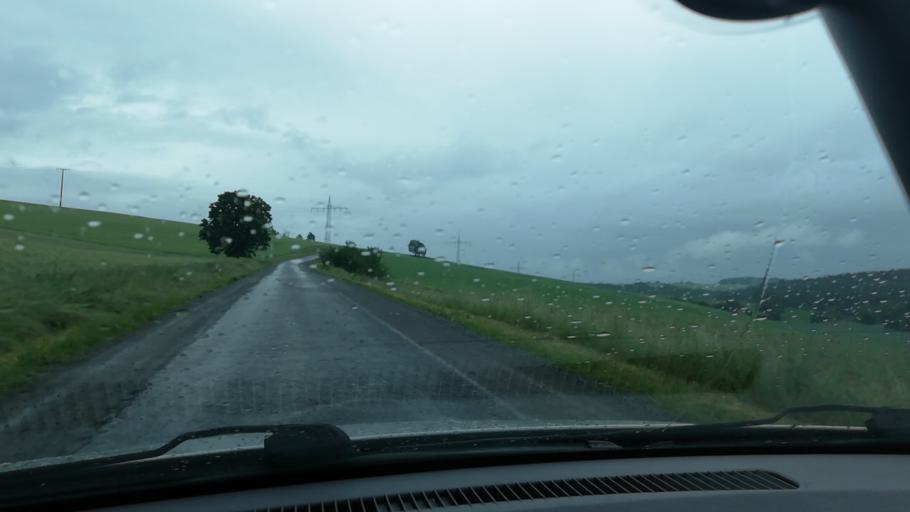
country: DE
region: Bavaria
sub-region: Regierungsbezirk Unterfranken
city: Hammelburg
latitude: 50.0311
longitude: 9.8968
